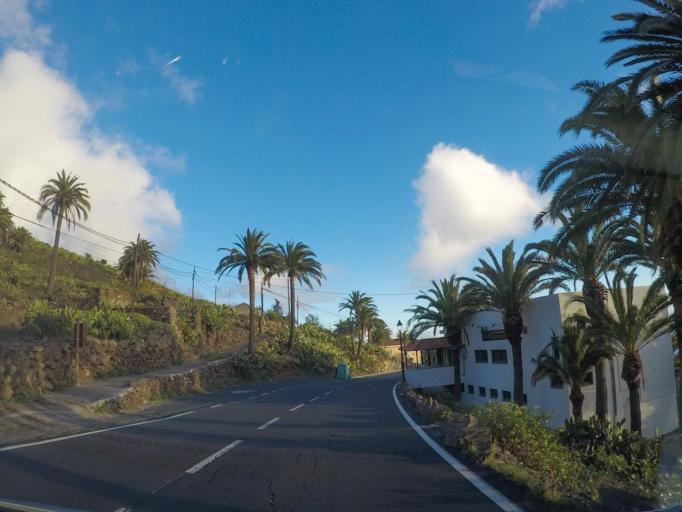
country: ES
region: Canary Islands
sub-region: Provincia de Santa Cruz de Tenerife
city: Alajero
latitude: 28.0601
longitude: -17.2355
